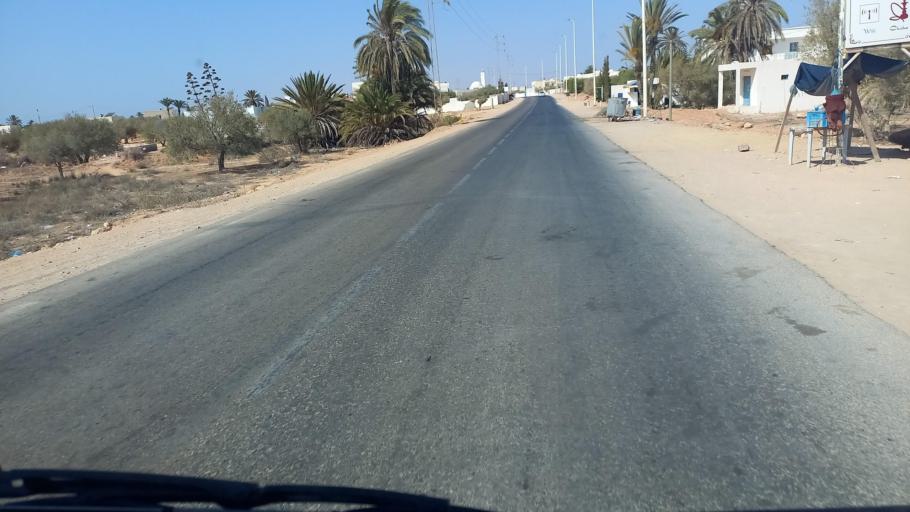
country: TN
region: Madanin
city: Midoun
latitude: 33.7767
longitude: 11.0334
